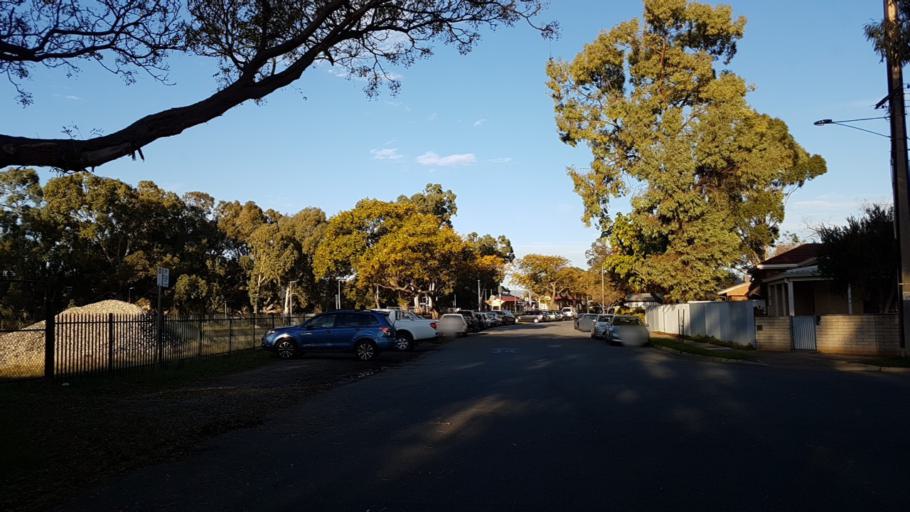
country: AU
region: South Australia
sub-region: Charles Sturt
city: Woodville North
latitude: -34.8762
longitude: 138.5360
